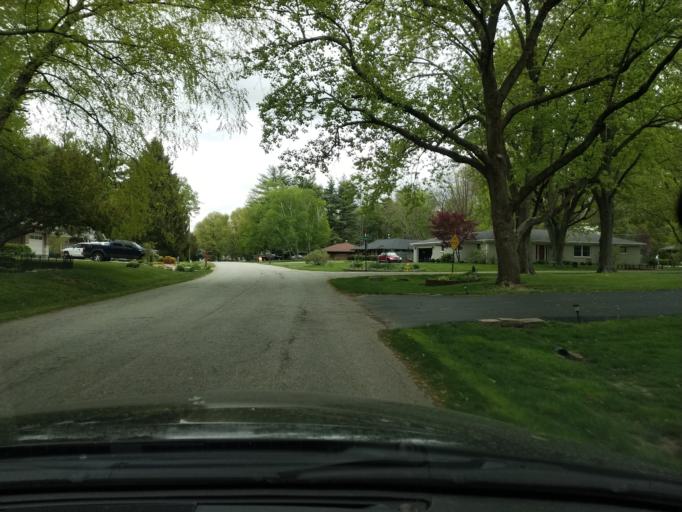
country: US
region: Indiana
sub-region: Hamilton County
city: Carmel
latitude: 39.9299
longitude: -86.1197
